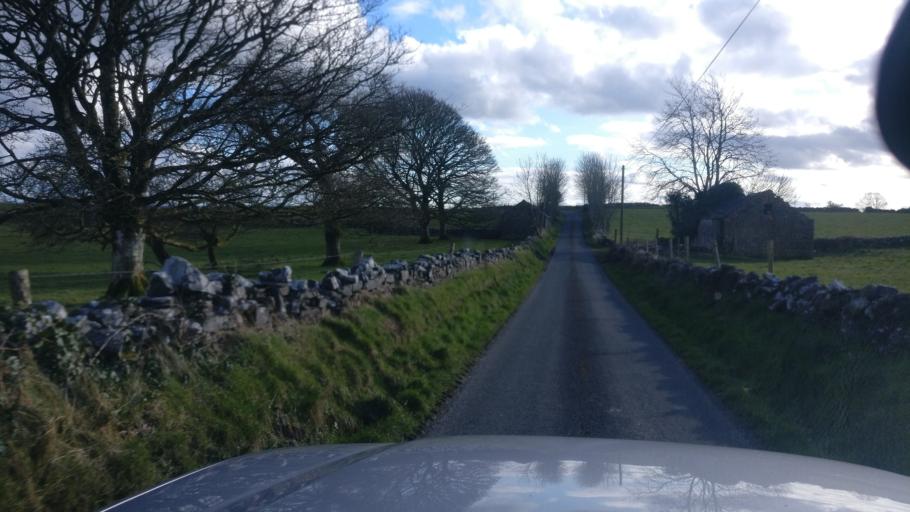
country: IE
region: Connaught
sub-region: County Galway
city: Loughrea
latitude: 53.1750
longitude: -8.4268
